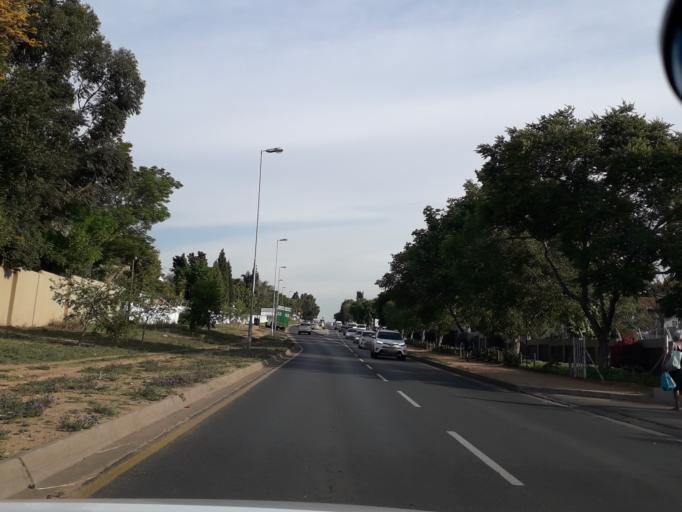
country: ZA
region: Gauteng
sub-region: City of Johannesburg Metropolitan Municipality
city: Diepsloot
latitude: -26.0368
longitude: 27.9935
